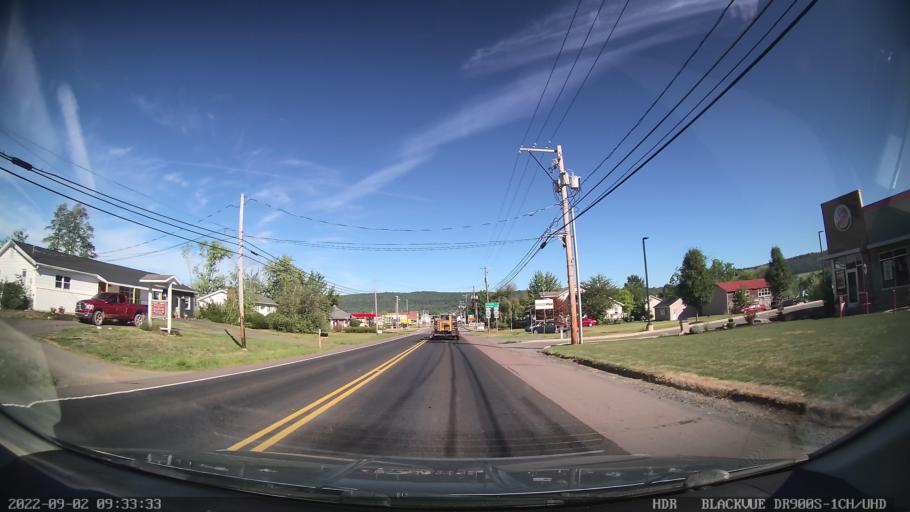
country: US
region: Pennsylvania
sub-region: Northumberland County
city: Elysburg
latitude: 40.8595
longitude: -76.5471
